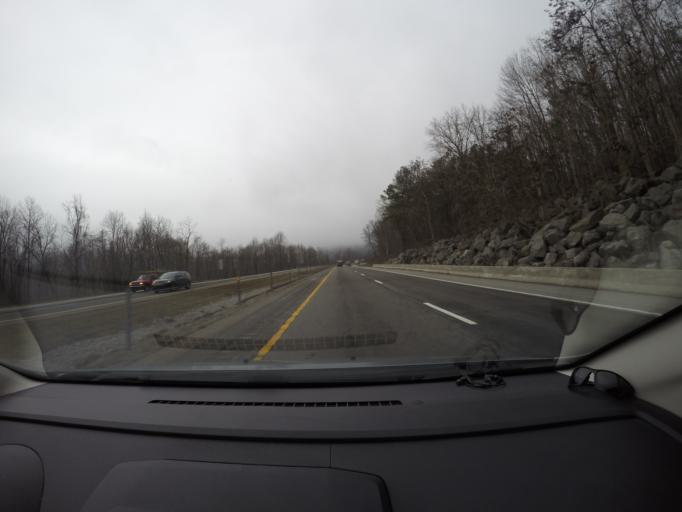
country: US
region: Tennessee
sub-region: Marion County
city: Monteagle
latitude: 35.2489
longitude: -85.8732
